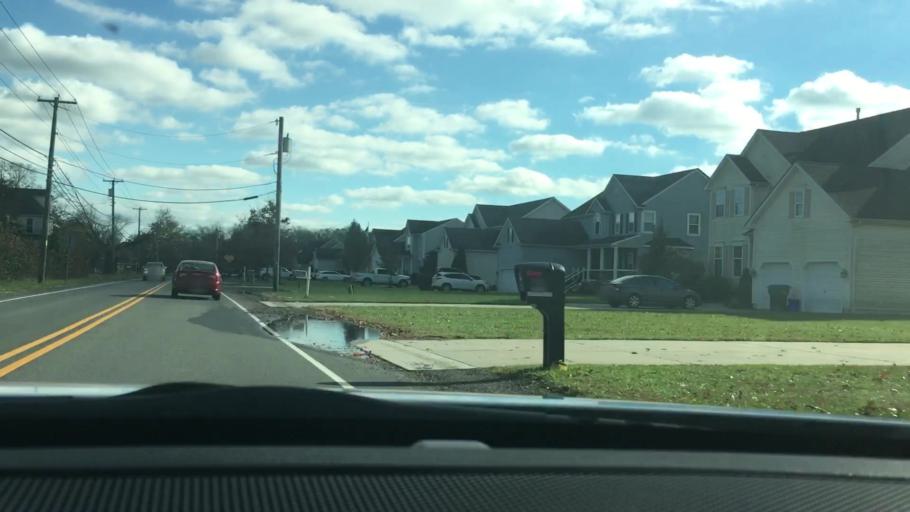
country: US
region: New Jersey
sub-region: Atlantic County
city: Northfield
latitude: 39.3775
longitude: -74.5744
